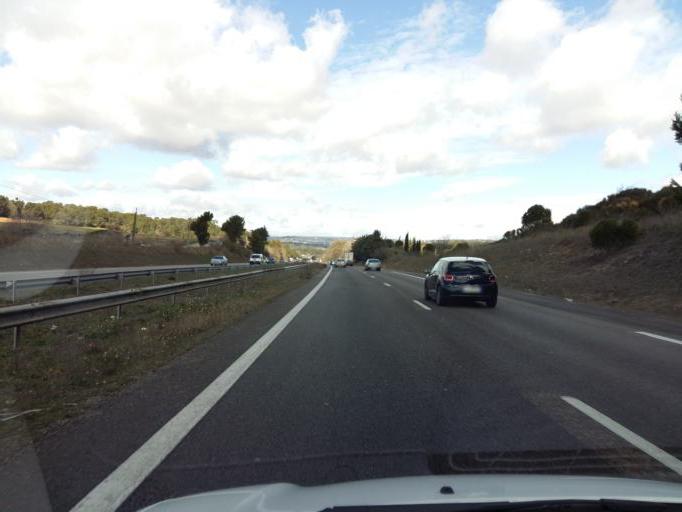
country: FR
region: Provence-Alpes-Cote d'Azur
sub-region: Departement des Bouches-du-Rhone
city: Bouc-Bel-Air
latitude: 43.4804
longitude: 5.4086
